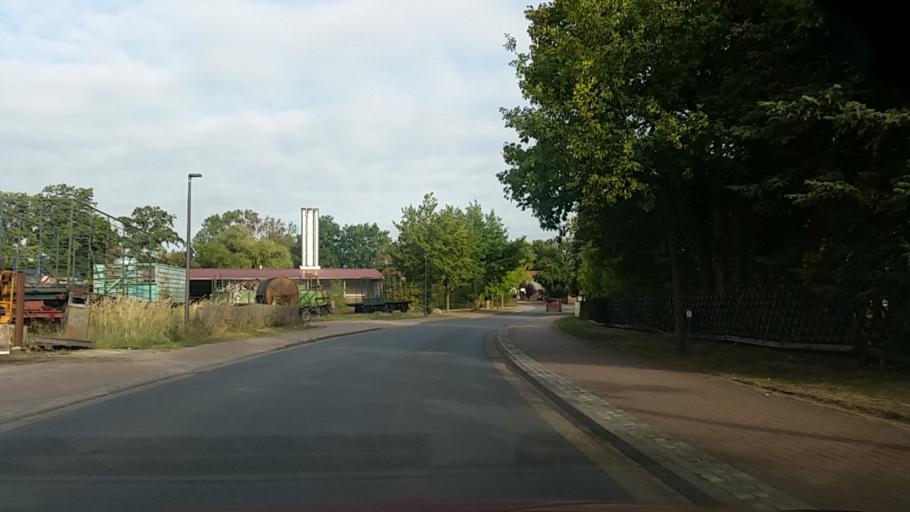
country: DE
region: Lower Saxony
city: Ahnsbeck
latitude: 52.6090
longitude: 10.2868
